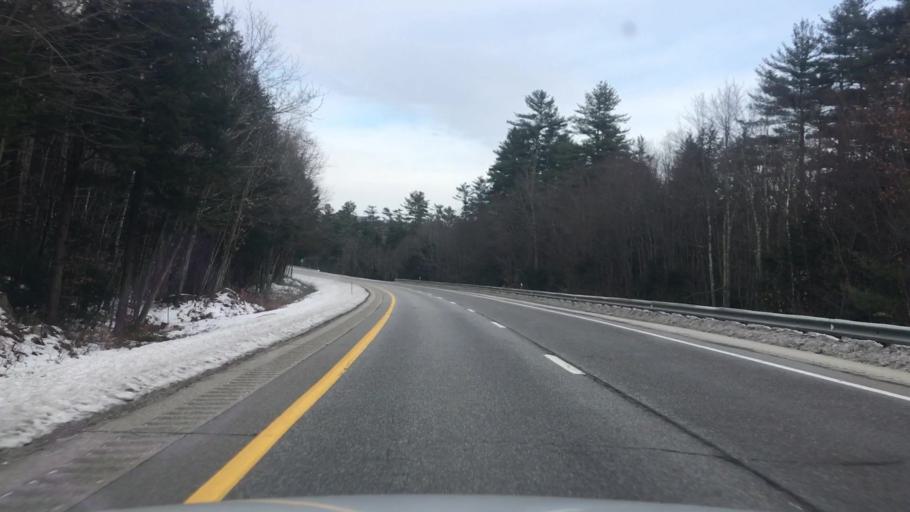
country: US
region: New Hampshire
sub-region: Merrimack County
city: Sutton
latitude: 43.3088
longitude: -71.8442
